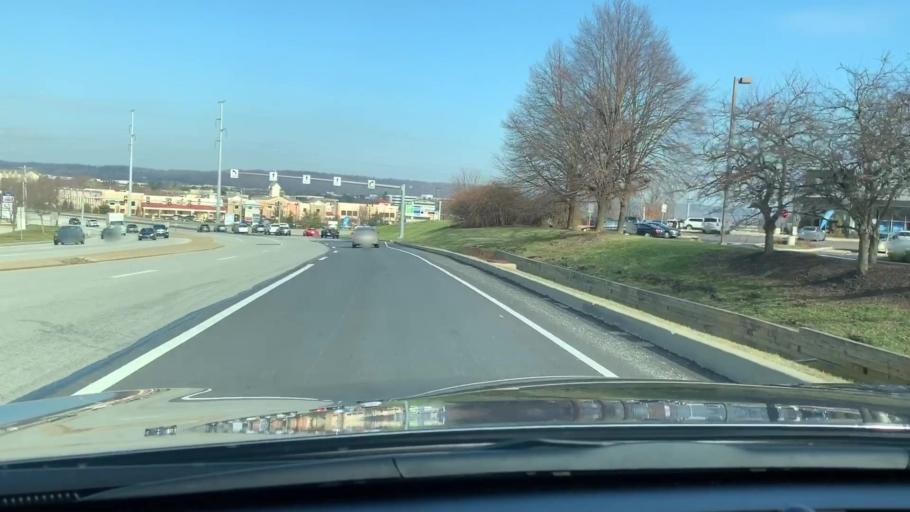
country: US
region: Pennsylvania
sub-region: Chester County
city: Malvern
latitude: 40.0446
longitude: -75.5234
